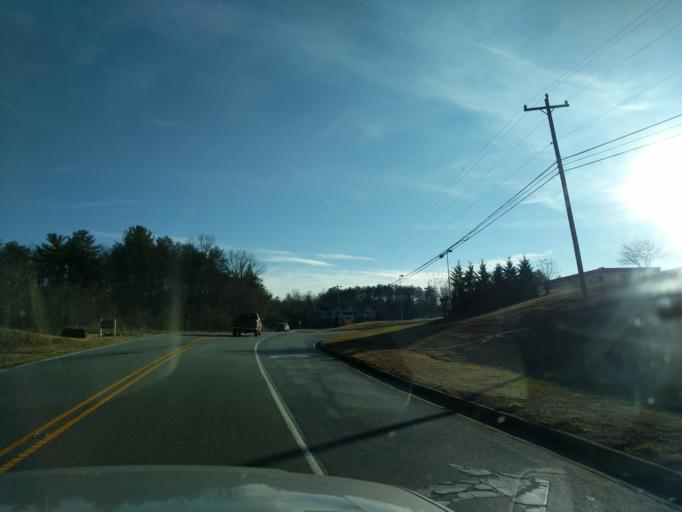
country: US
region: North Carolina
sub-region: Rutherford County
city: Lake Lure
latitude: 35.4116
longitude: -82.1966
